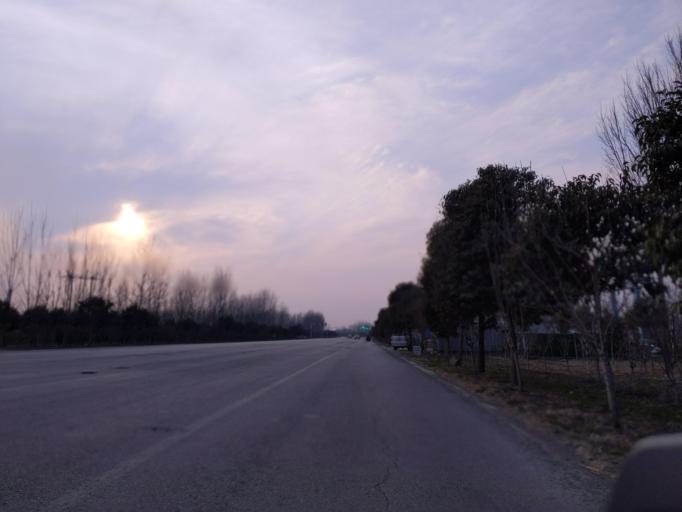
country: CN
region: Henan Sheng
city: Puyang
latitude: 35.8199
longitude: 114.9841
